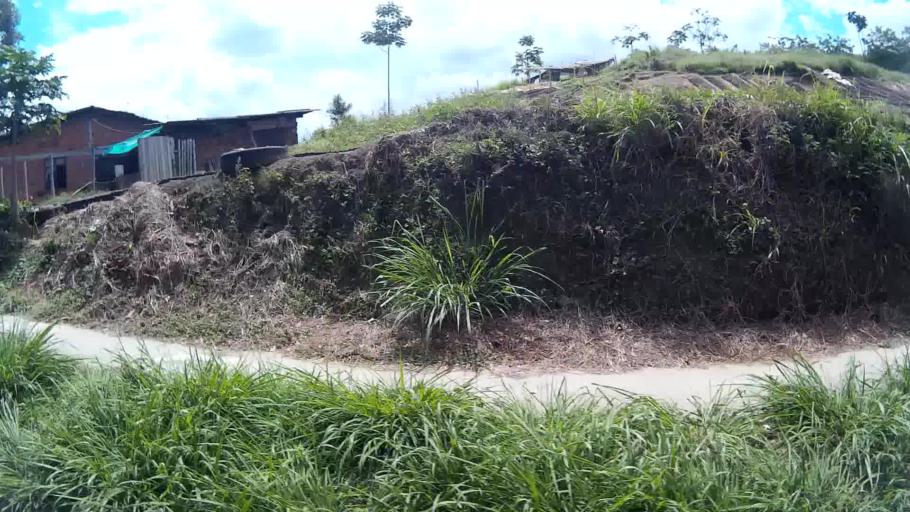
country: CO
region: Risaralda
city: Pereira
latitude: 4.8087
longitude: -75.7664
